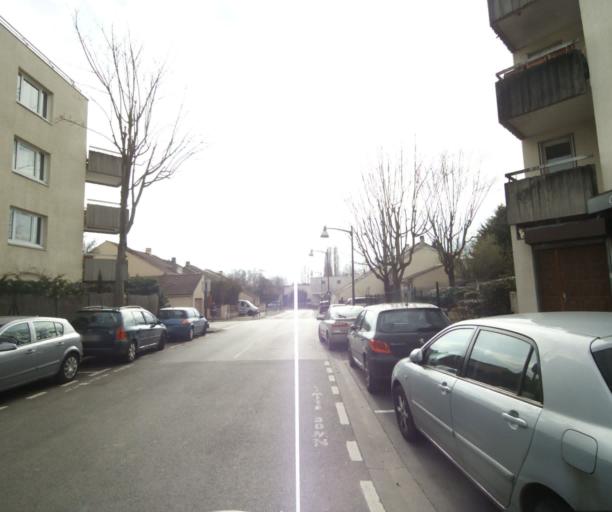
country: FR
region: Ile-de-France
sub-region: Departement du Val-d'Oise
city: Vaureal
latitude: 49.0465
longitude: 2.0447
